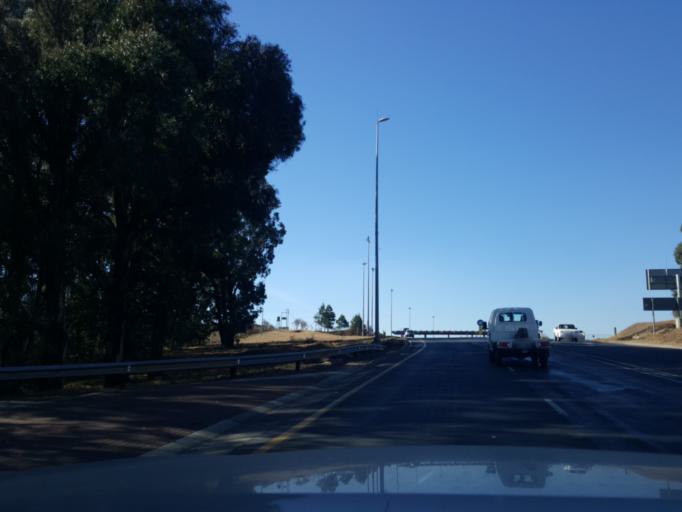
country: ZA
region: Mpumalanga
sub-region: Nkangala District Municipality
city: Belfast
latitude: -25.6306
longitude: 30.2563
